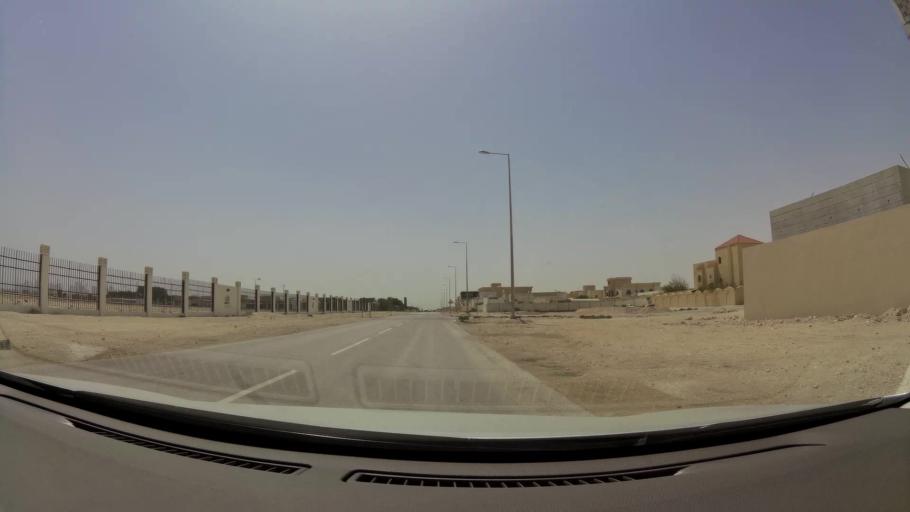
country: QA
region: Baladiyat Umm Salal
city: Umm Salal Muhammad
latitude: 25.3657
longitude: 51.4790
